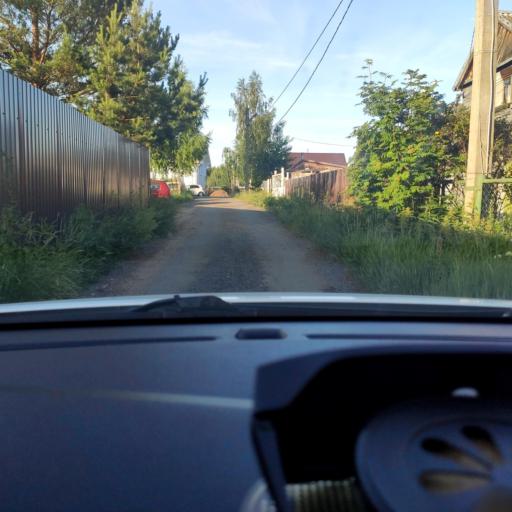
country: RU
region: Tatarstan
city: Stolbishchi
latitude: 55.6953
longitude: 49.1918
